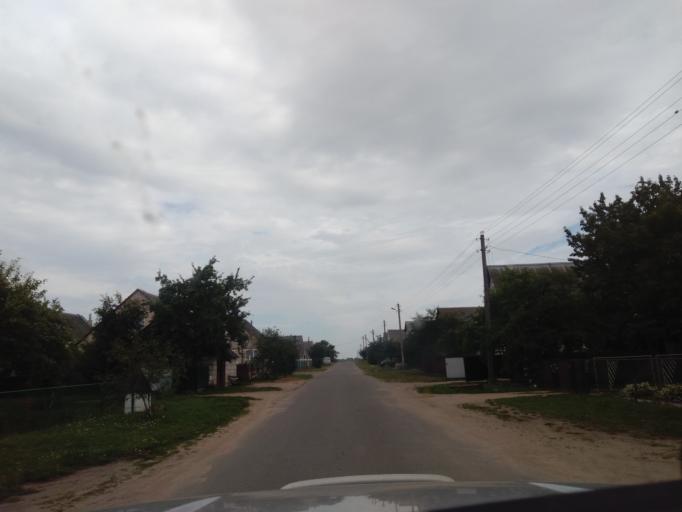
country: BY
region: Minsk
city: Kapyl'
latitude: 53.1563
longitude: 27.0690
